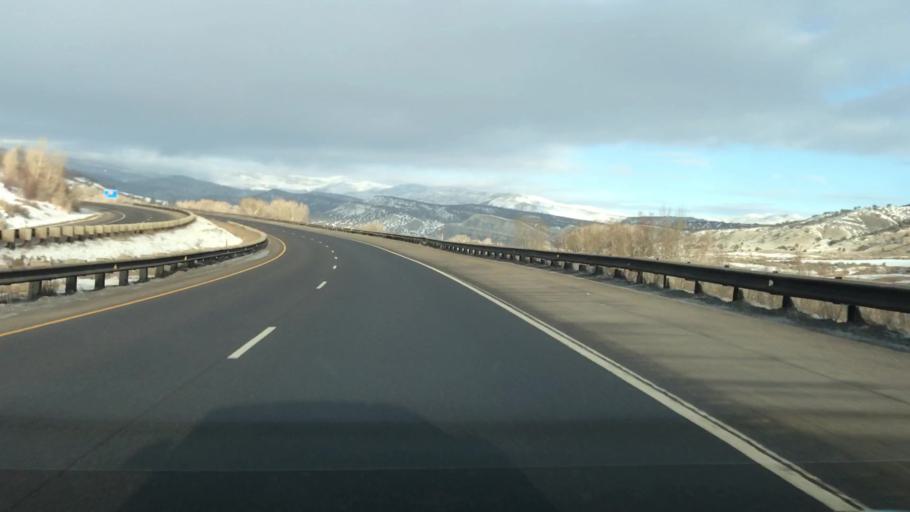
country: US
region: Colorado
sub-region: Eagle County
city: Edwards
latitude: 39.6812
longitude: -106.6493
